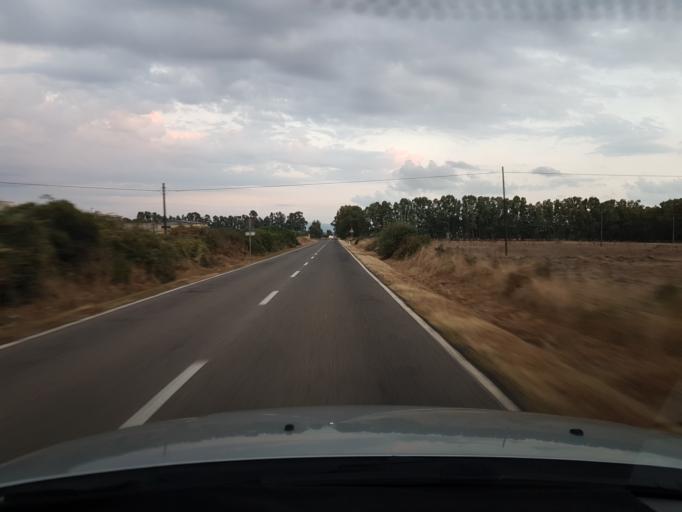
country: IT
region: Sardinia
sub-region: Provincia di Oristano
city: Milis
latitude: 40.0366
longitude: 8.6376
